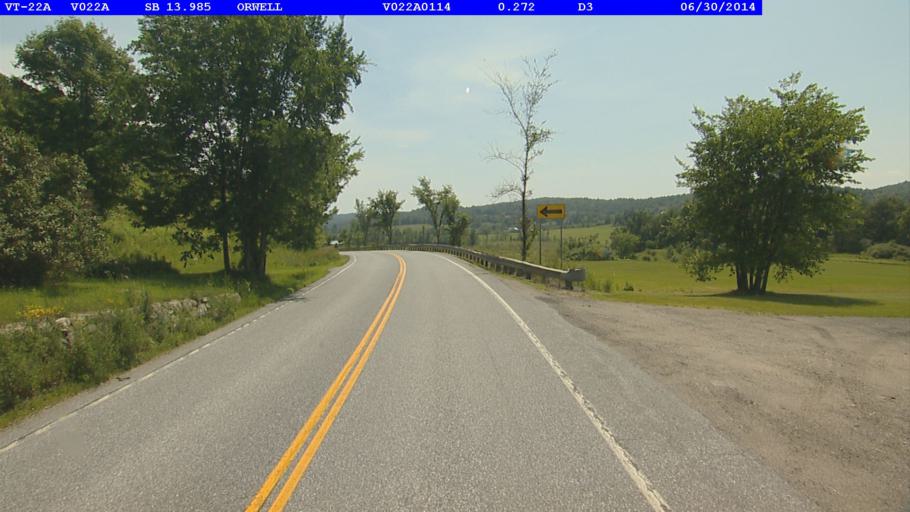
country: US
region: New York
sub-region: Essex County
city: Ticonderoga
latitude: 43.7612
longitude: -73.3125
